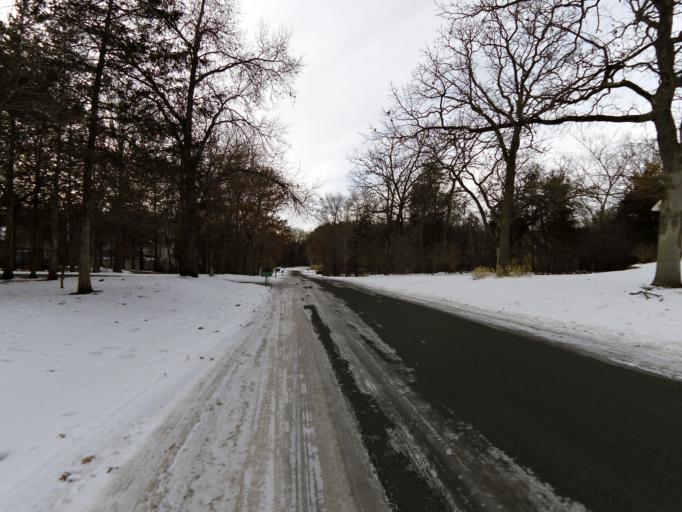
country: US
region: Minnesota
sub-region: Washington County
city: Lake Saint Croix Beach
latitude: 44.9109
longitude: -92.7734
